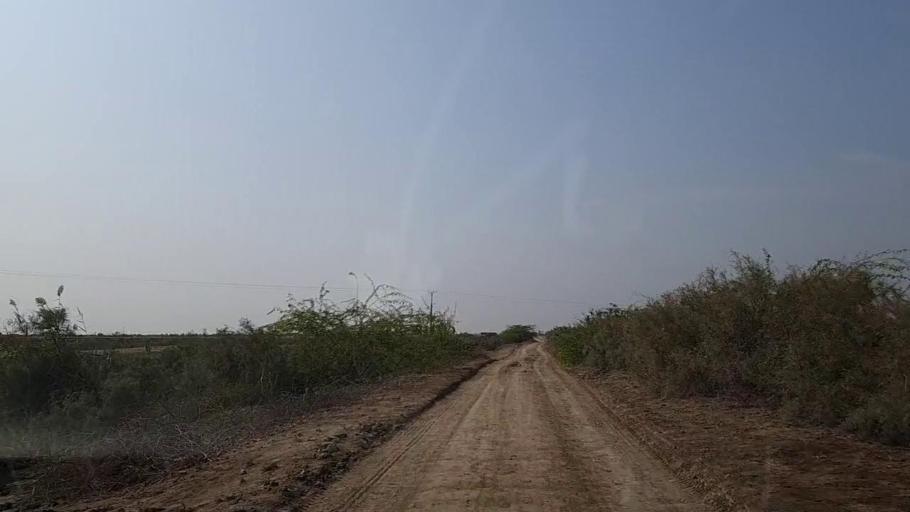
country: PK
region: Sindh
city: Gharo
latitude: 24.6735
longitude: 67.7034
